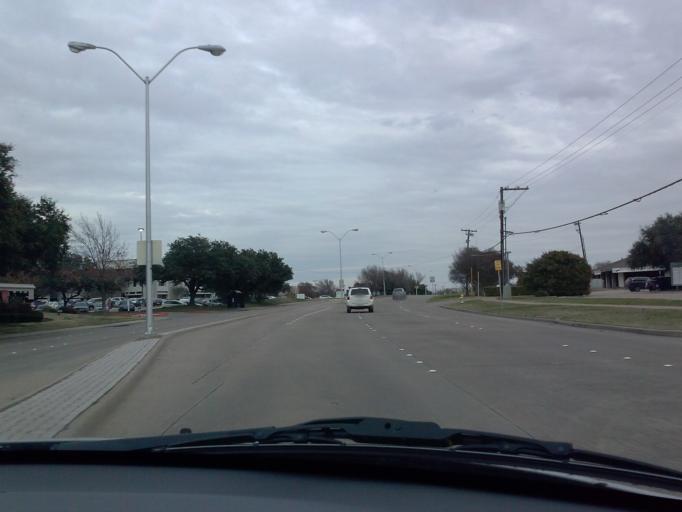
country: US
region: Texas
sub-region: Collin County
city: Plano
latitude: 33.0191
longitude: -96.7665
